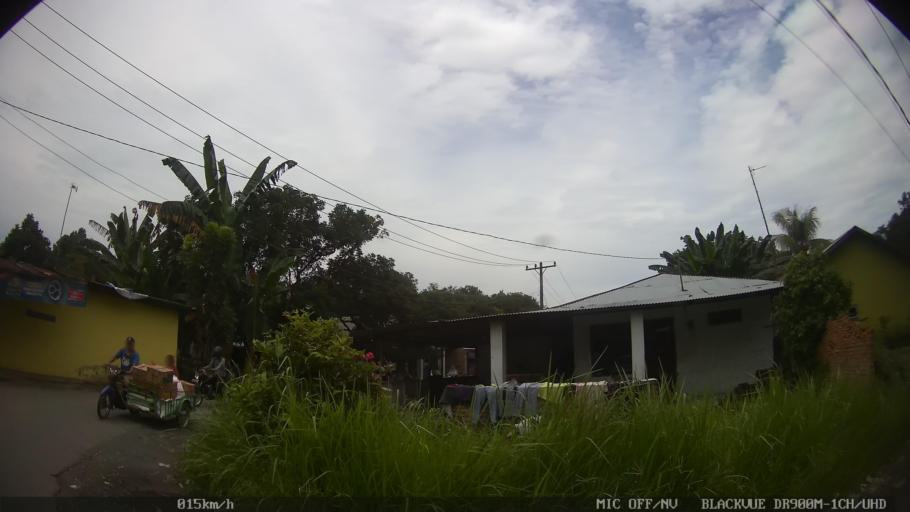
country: ID
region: North Sumatra
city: Sunggal
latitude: 3.6351
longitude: 98.5914
